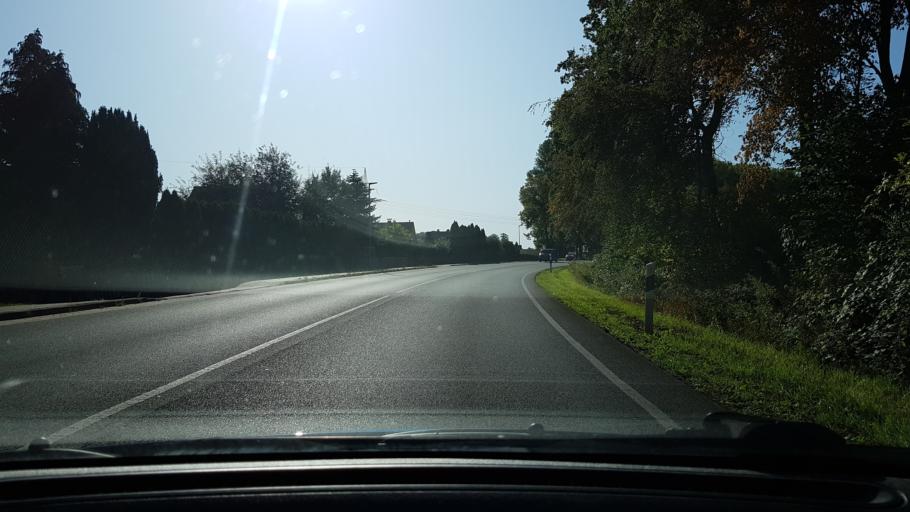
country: DE
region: Lower Saxony
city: Bad Munder am Deister
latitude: 52.2279
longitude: 9.4344
